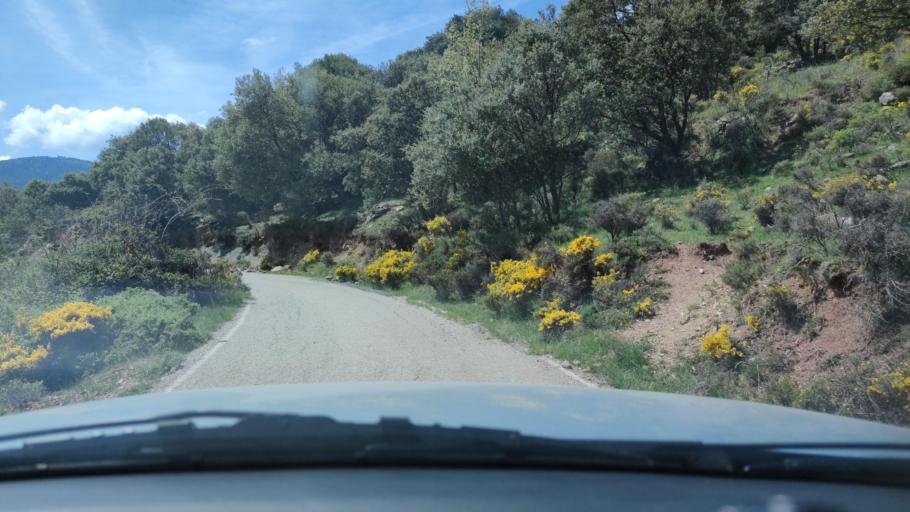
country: ES
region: Catalonia
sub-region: Provincia de Lleida
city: Sort
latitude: 42.3065
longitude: 1.1185
